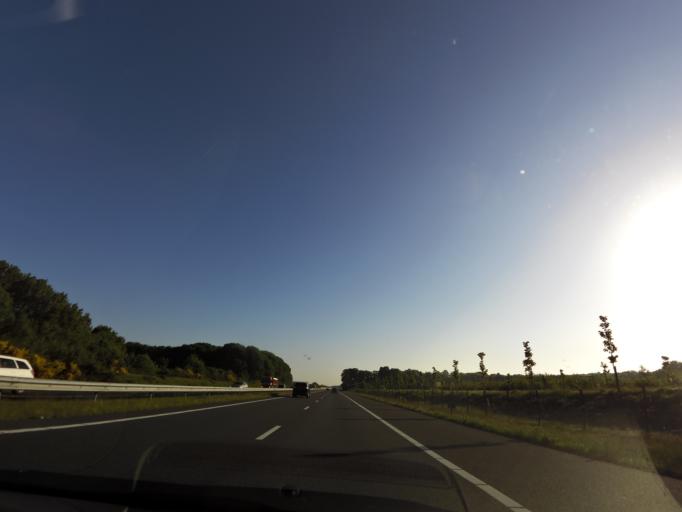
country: NL
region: Limburg
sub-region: Gemeente Beesel
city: Beesel
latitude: 51.2529
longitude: 6.0559
